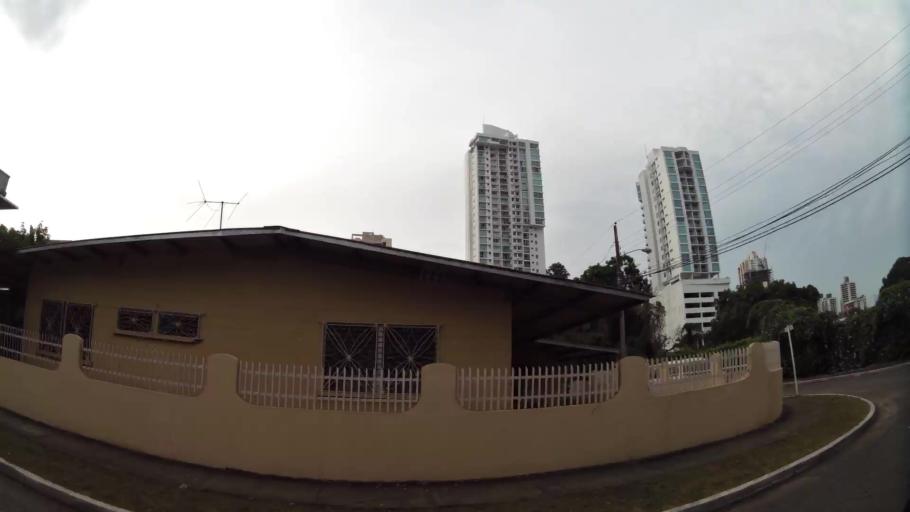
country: PA
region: Panama
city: Panama
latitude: 9.0089
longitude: -79.5108
